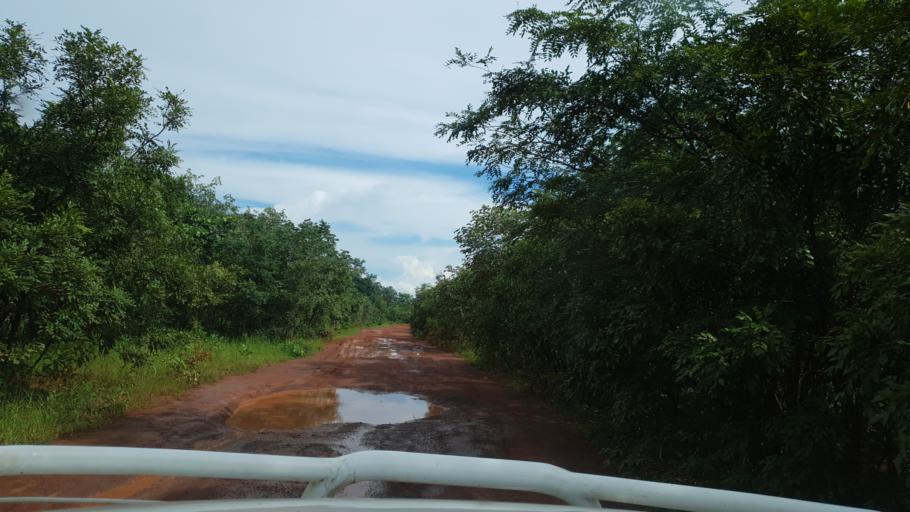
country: ML
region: Sikasso
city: Kolondieba
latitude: 10.7442
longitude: -6.9118
